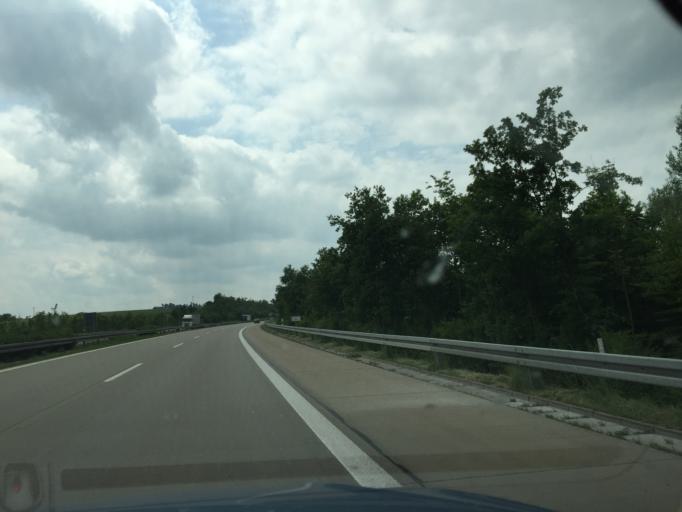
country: DE
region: Bavaria
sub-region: Regierungsbezirk Mittelfranken
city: Schopfloch
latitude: 49.1103
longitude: 10.2289
